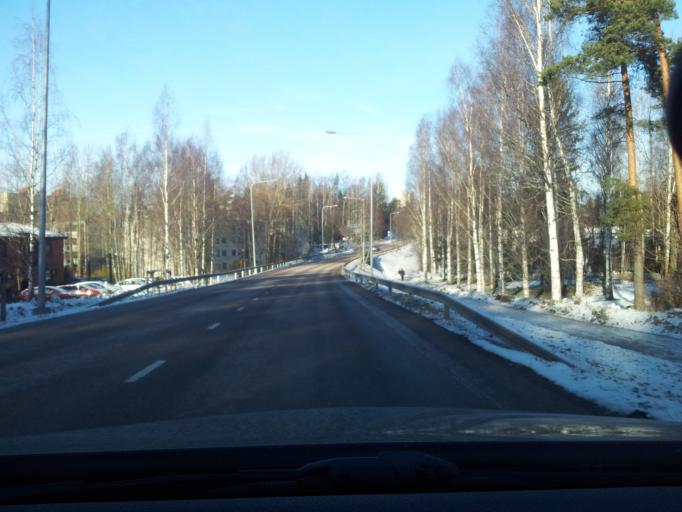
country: FI
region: Uusimaa
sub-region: Helsinki
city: Koukkuniemi
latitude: 60.1522
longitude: 24.7490
